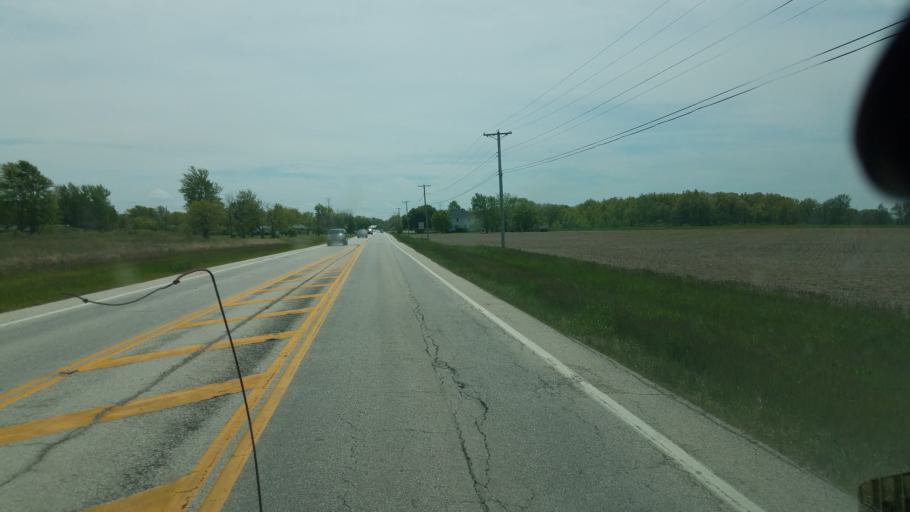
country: US
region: Ohio
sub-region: Ottawa County
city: Oak Harbor
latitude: 41.5655
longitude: -83.0788
